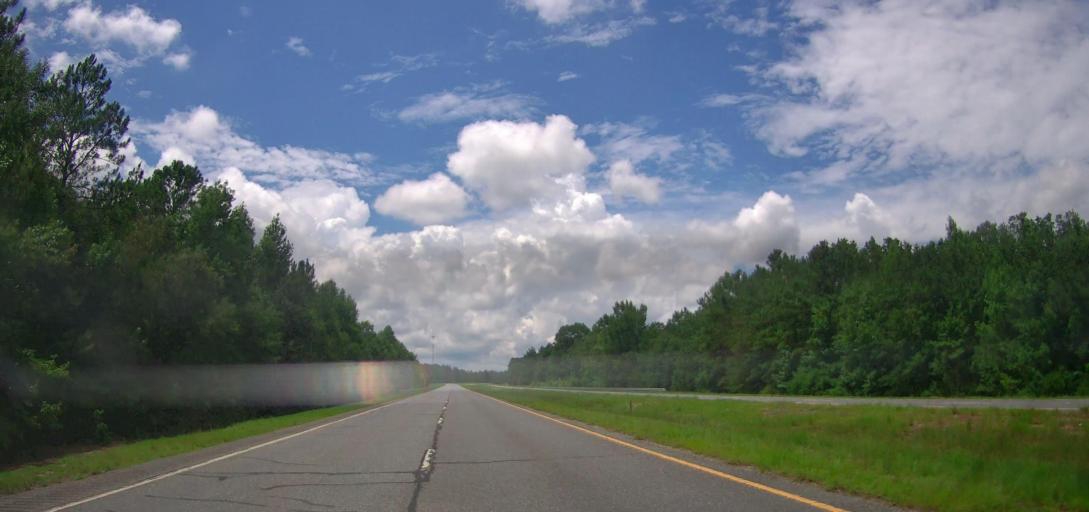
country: US
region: Georgia
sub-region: Dodge County
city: Eastman
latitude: 32.1830
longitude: -83.1957
